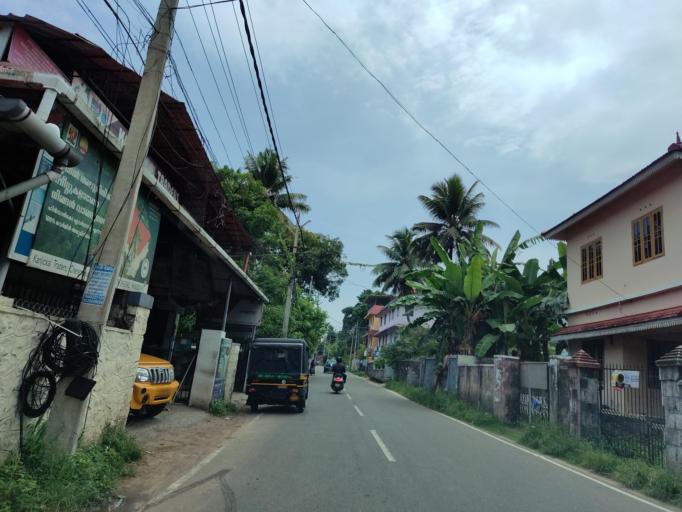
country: IN
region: Kerala
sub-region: Alappuzha
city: Chengannur
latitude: 9.3173
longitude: 76.6119
